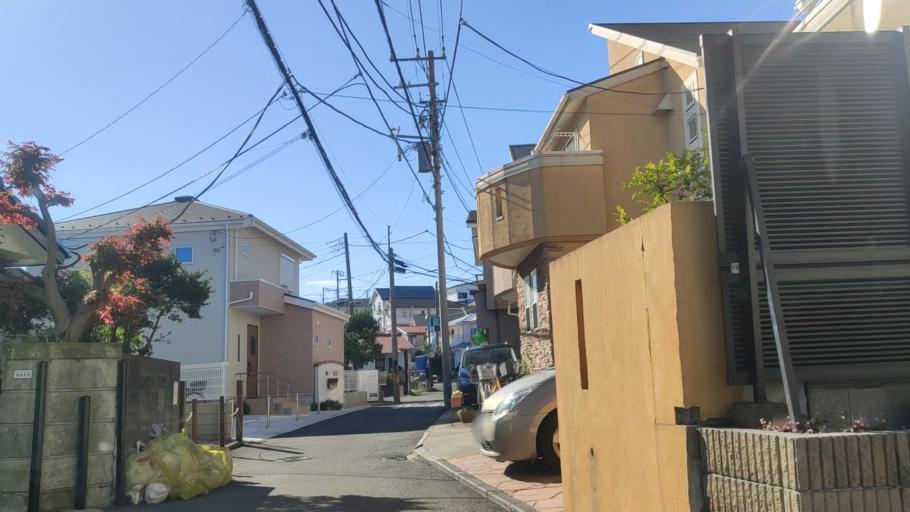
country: JP
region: Kanagawa
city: Yokohama
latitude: 35.4268
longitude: 139.6555
